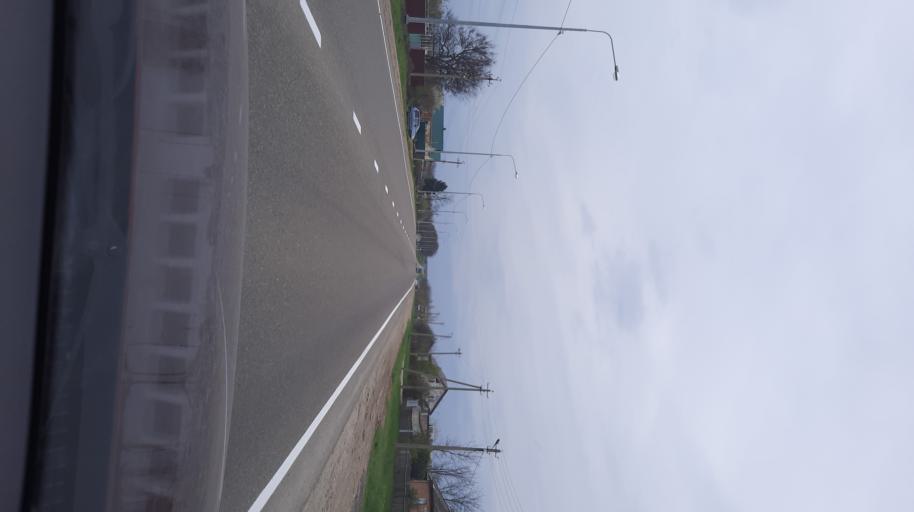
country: RU
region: Krasnodarskiy
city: Dneprovskaya
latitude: 45.6749
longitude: 38.8503
